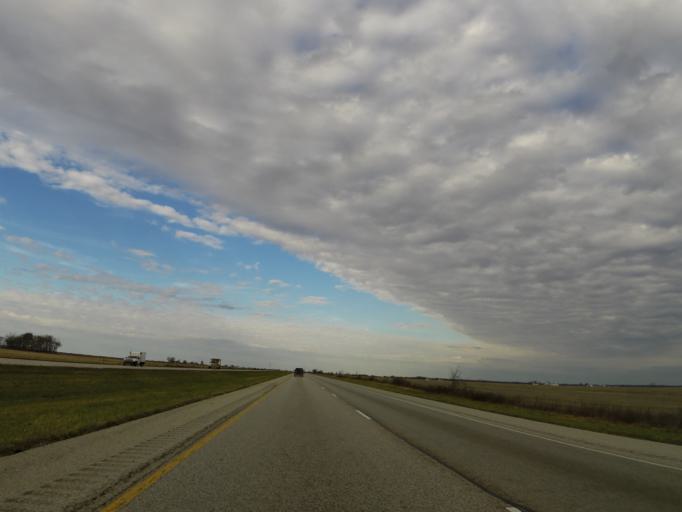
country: US
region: Illinois
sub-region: Washington County
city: Nashville
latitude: 38.4189
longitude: -89.4467
